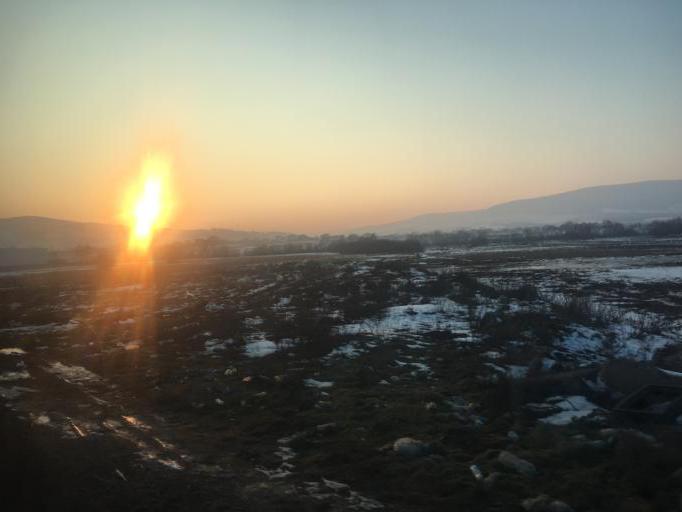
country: XK
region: Pristina
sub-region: Komuna e Drenasit
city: Glogovac
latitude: 42.5819
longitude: 20.8960
